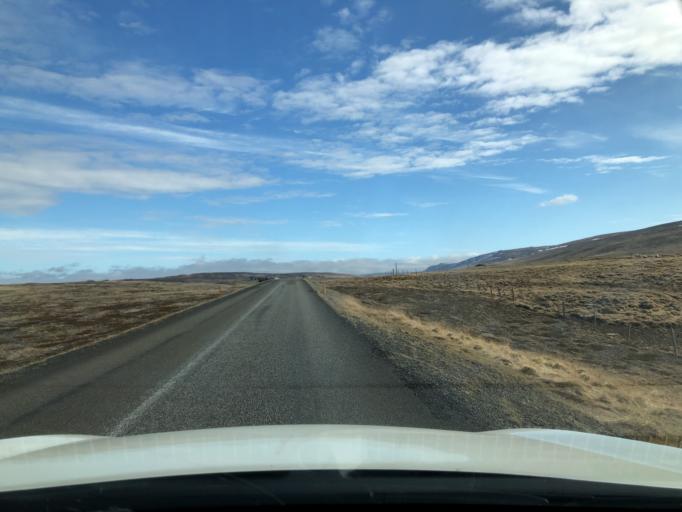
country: IS
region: West
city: Borgarnes
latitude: 65.1056
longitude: -21.7053
